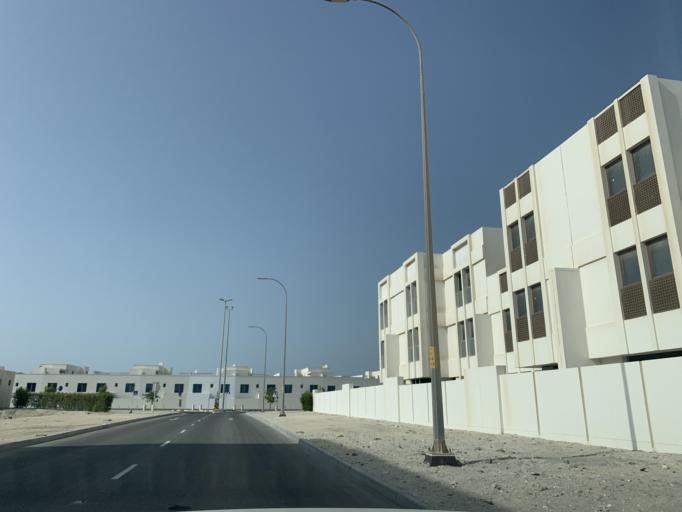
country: BH
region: Muharraq
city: Al Muharraq
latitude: 26.3118
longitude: 50.6356
